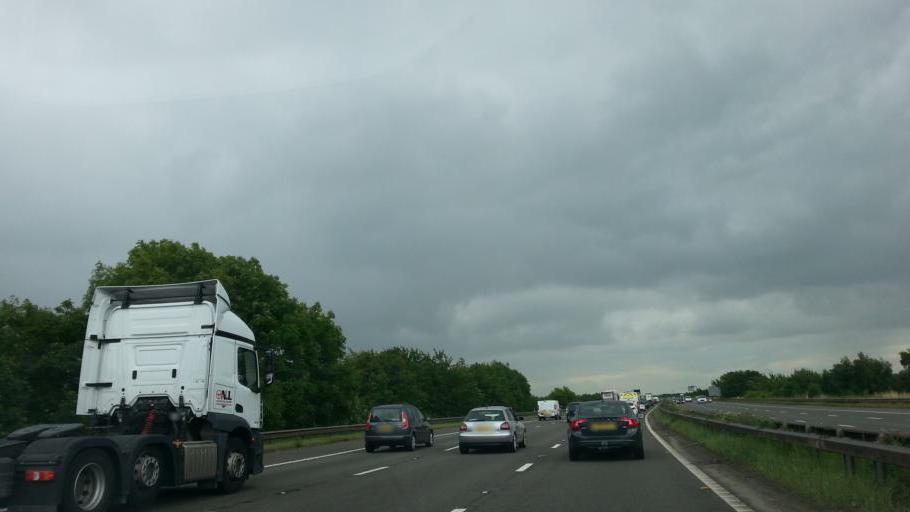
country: GB
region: England
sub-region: City and Borough of Wakefield
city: Normanton
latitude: 53.7246
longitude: -1.4318
